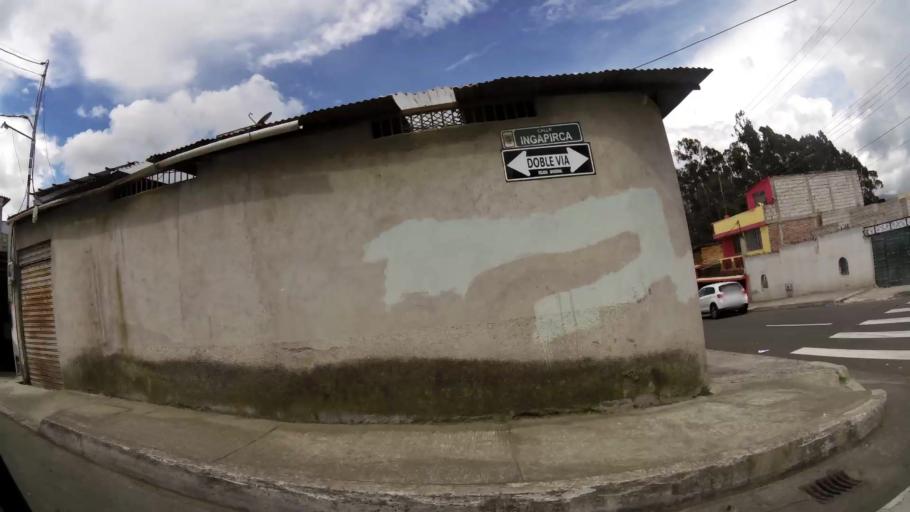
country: EC
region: Tungurahua
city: Ambato
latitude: -1.2622
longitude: -78.6103
